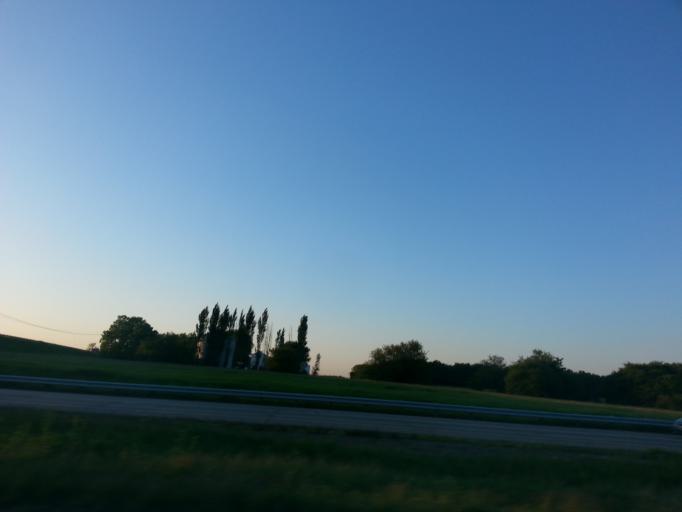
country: US
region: Indiana
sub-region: Fountain County
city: Veedersburg
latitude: 40.1195
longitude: -87.1480
